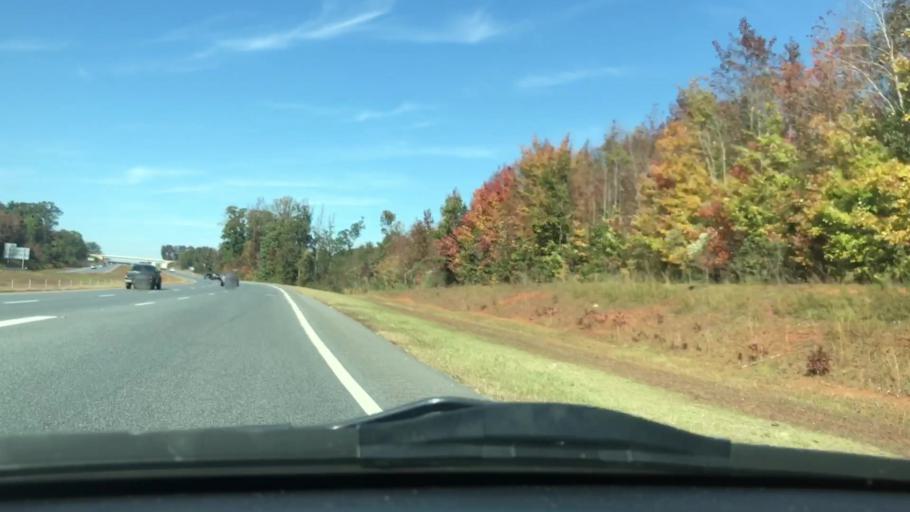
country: US
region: North Carolina
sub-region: Randolph County
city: Randleman
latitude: 35.8252
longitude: -79.8554
